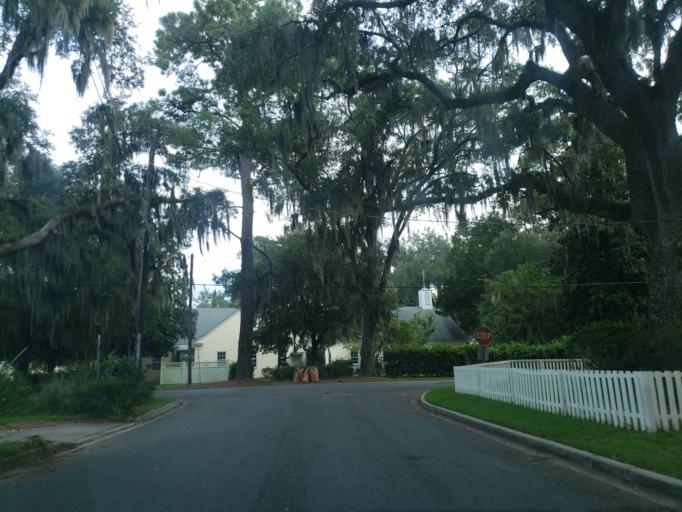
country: US
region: Georgia
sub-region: Chatham County
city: Isle of Hope
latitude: 31.9840
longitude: -81.0579
